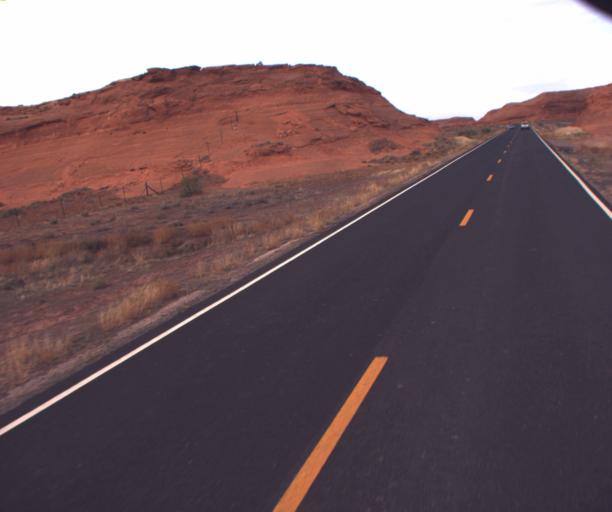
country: US
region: Arizona
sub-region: Apache County
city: Many Farms
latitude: 36.7620
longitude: -109.6508
